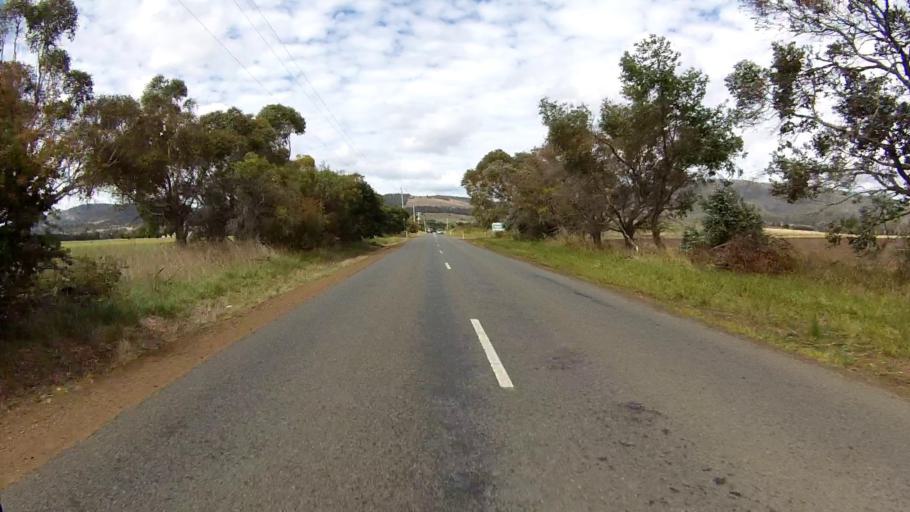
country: AU
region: Tasmania
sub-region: Clarence
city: Cambridge
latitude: -42.7535
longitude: 147.4082
